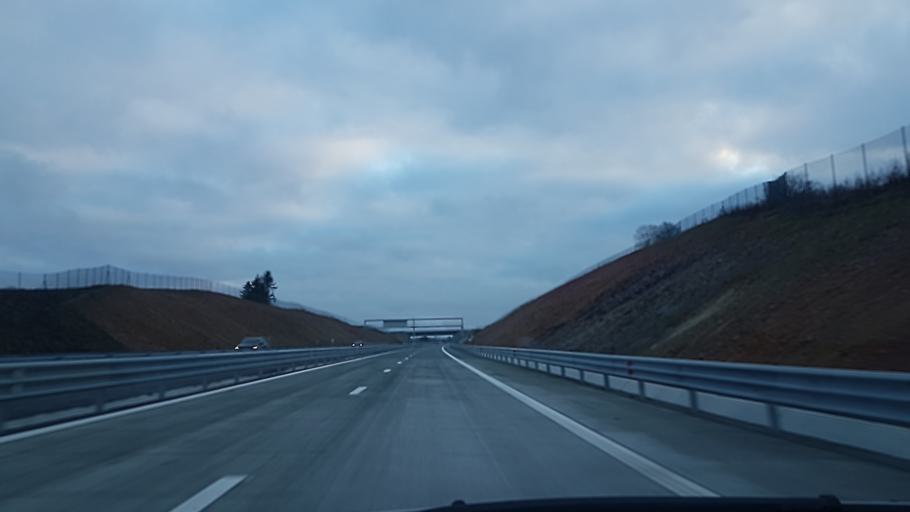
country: FR
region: Champagne-Ardenne
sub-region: Departement des Ardennes
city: Rocroi
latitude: 49.9710
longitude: 4.5376
